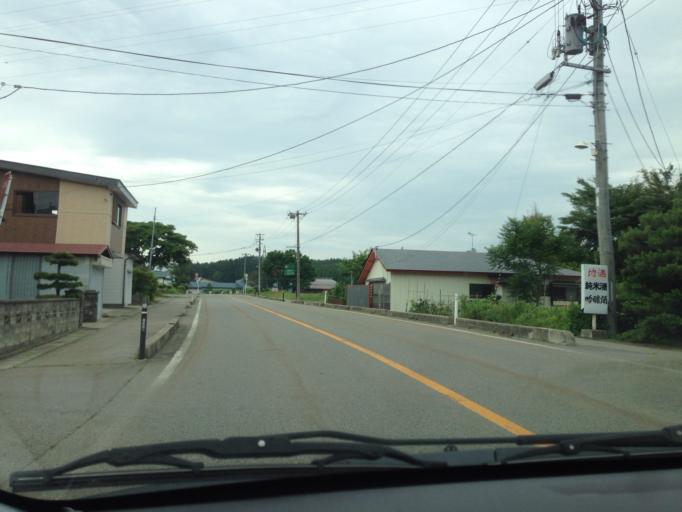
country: JP
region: Fukushima
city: Inawashiro
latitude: 37.5514
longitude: 140.0560
